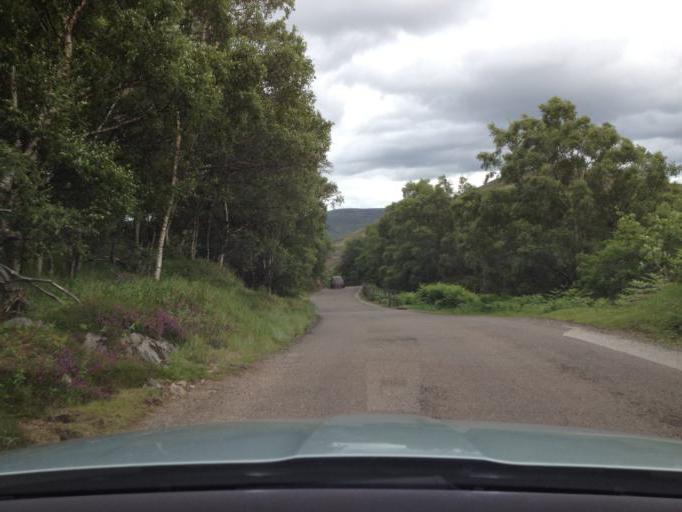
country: GB
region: Scotland
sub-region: Aberdeenshire
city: Aboyne
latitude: 56.8909
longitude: -2.7762
